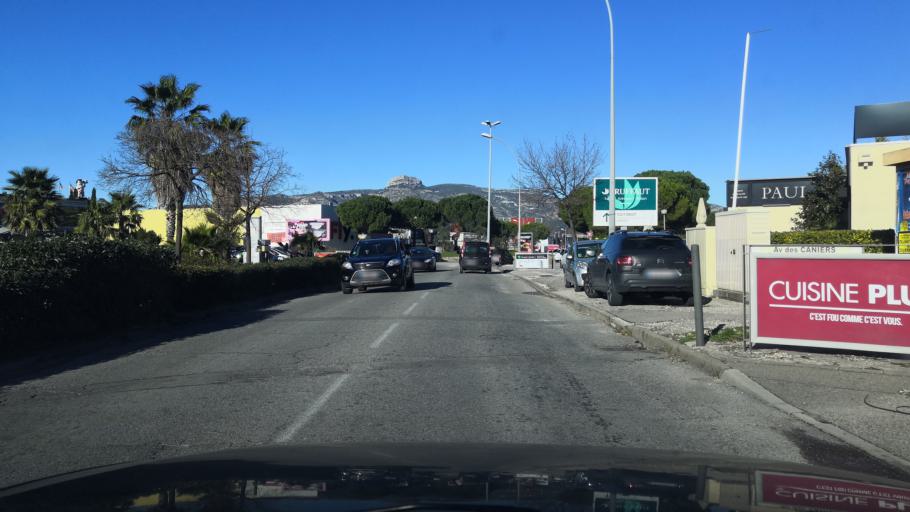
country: FR
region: Provence-Alpes-Cote d'Azur
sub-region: Departement des Bouches-du-Rhone
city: Aubagne
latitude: 43.2889
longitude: 5.5939
